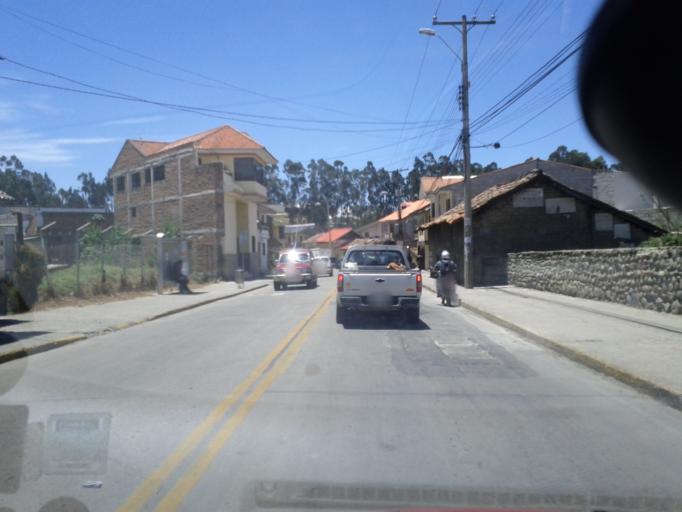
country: EC
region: Azuay
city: Cuenca
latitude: -2.9084
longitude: -79.0270
